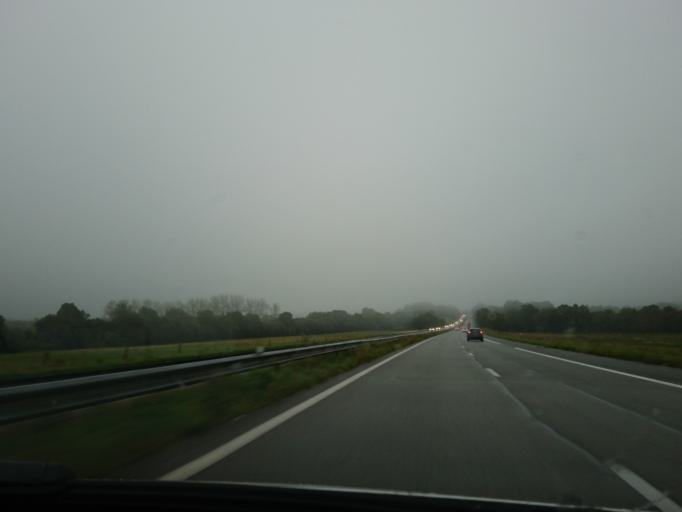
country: FR
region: Brittany
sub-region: Departement du Finistere
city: Landrevarzec
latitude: 48.0678
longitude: -4.0485
